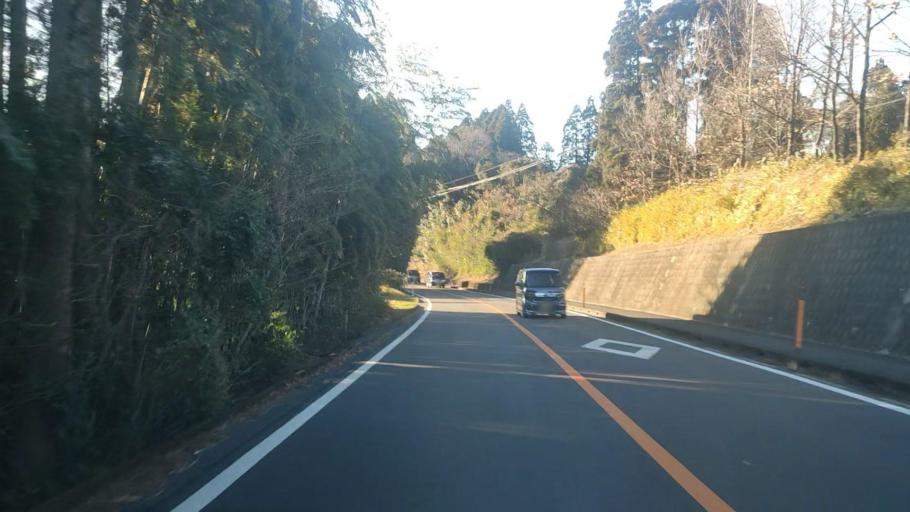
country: JP
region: Miyazaki
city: Miyazaki-shi
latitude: 31.8592
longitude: 131.3741
